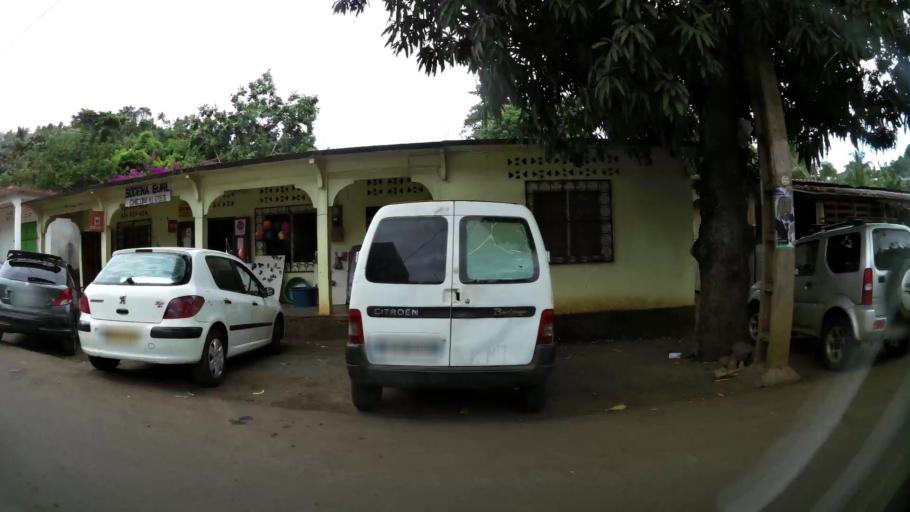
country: YT
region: Chiconi
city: Chiconi
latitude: -12.8402
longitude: 45.1214
